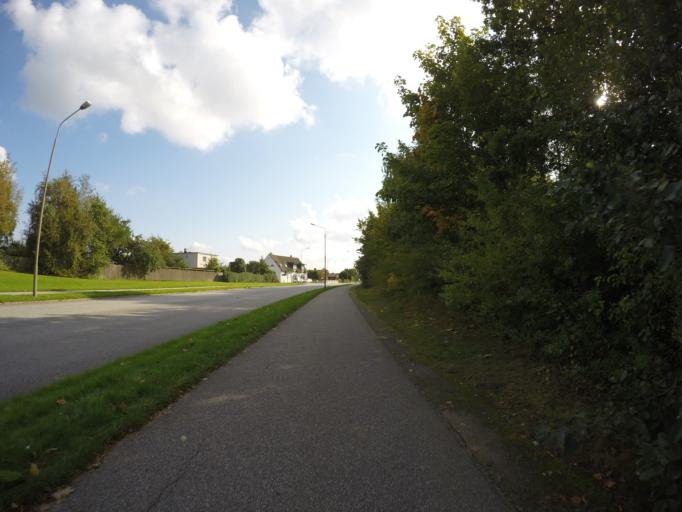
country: SE
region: Skane
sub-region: Burlovs Kommun
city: Arloev
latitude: 55.5965
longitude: 13.0738
